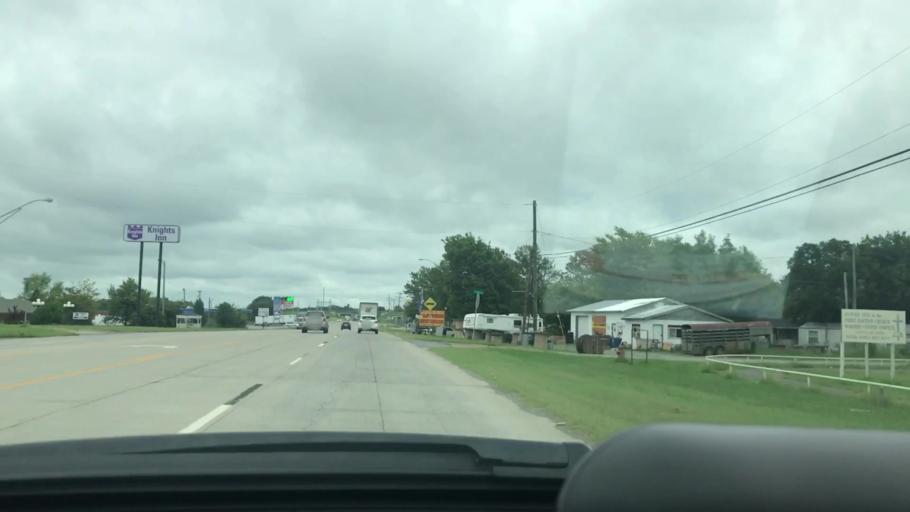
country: US
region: Oklahoma
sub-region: Pittsburg County
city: McAlester
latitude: 34.8309
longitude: -95.8410
